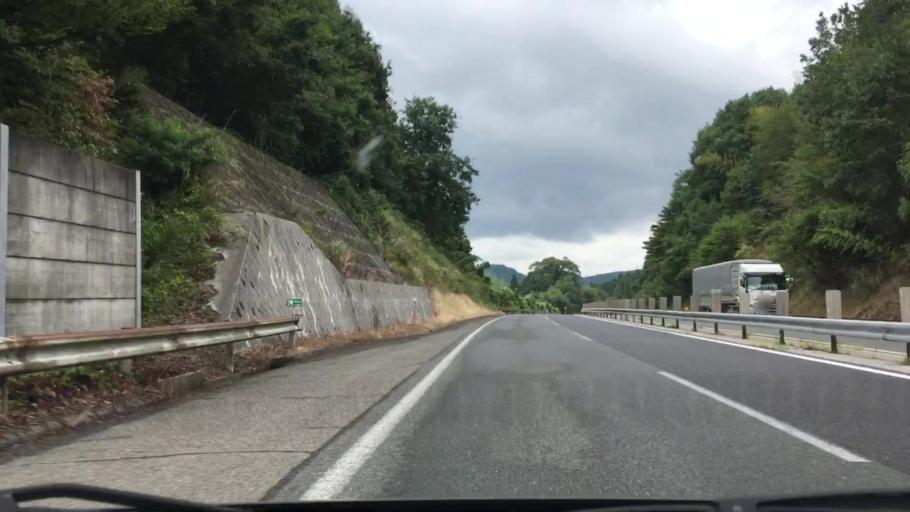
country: JP
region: Okayama
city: Niimi
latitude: 34.9350
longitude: 133.3281
